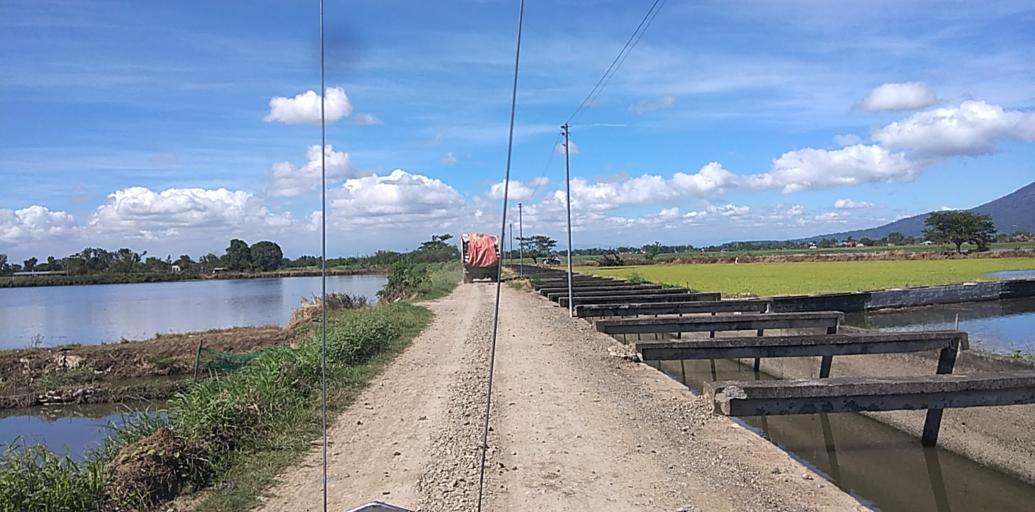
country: PH
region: Central Luzon
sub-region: Province of Pampanga
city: Candating
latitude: 15.1301
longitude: 120.8062
